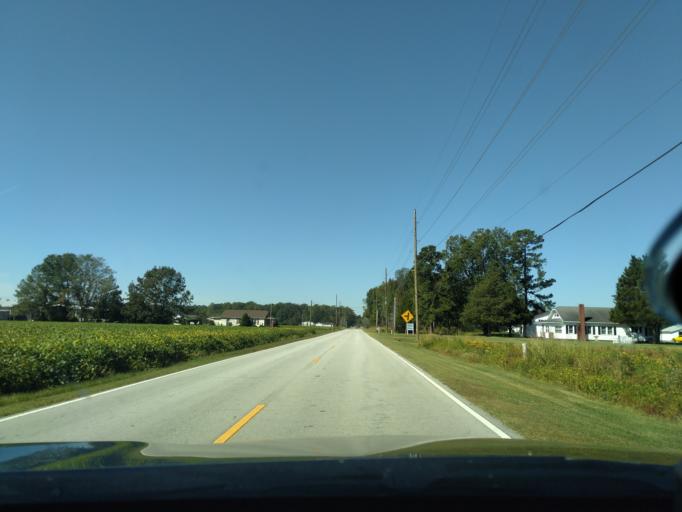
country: US
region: North Carolina
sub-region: Beaufort County
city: River Road
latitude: 35.5761
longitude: -76.9388
